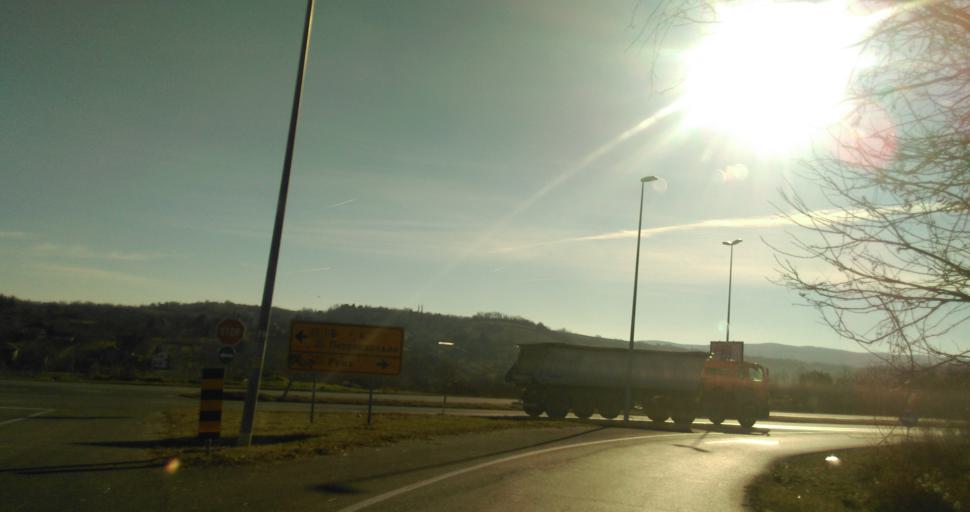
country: RS
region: Autonomna Pokrajina Vojvodina
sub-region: Juznobacki Okrug
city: Petrovaradin
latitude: 45.2222
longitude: 19.8695
